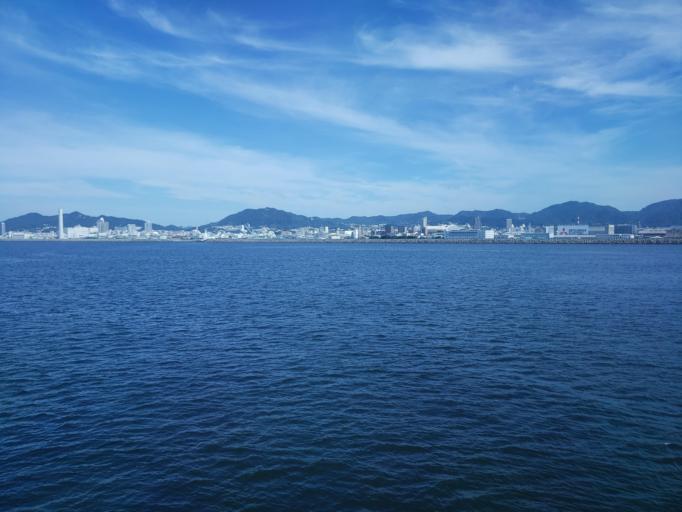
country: JP
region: Hyogo
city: Kobe
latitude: 34.6415
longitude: 135.1800
